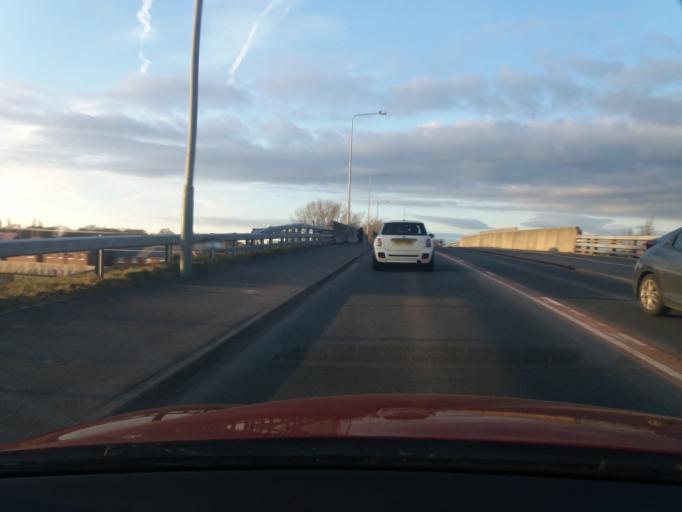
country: GB
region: England
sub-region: Lancashire
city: Euxton
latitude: 53.6730
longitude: -2.6634
